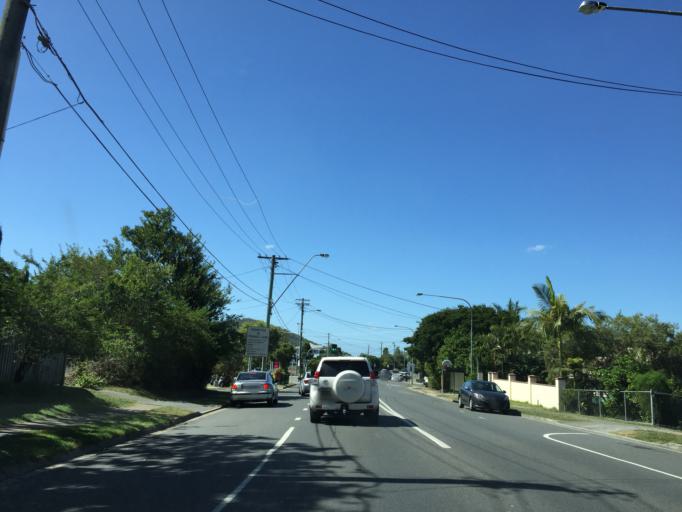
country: AU
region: Queensland
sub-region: Moreton Bay
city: Ferny Hills
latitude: -27.4431
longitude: 152.9427
